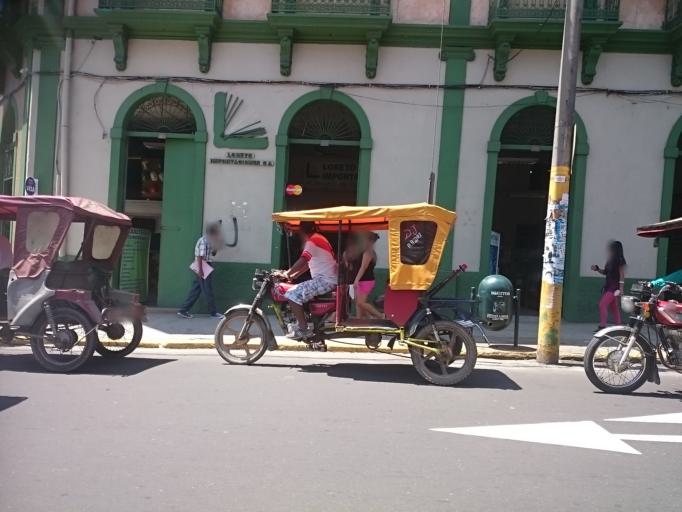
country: PE
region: Loreto
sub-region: Provincia de Maynas
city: Iquitos
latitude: -3.7544
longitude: -73.2469
